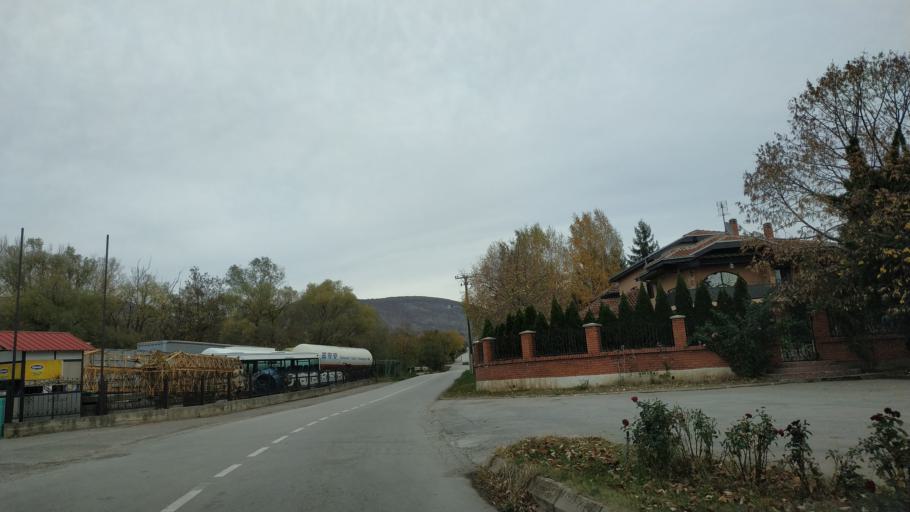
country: RS
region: Central Serbia
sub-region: Nisavski Okrug
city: Nis
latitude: 43.3576
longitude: 21.9503
